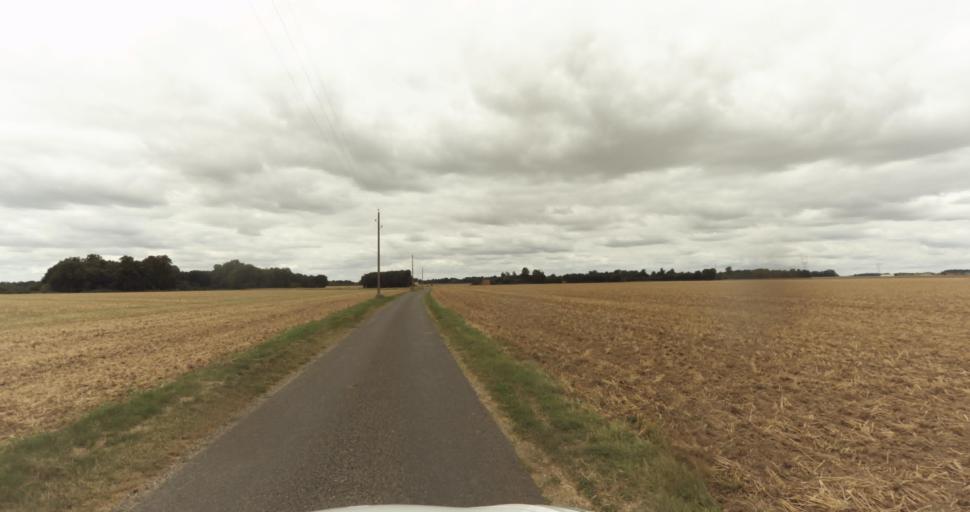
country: FR
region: Haute-Normandie
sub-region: Departement de l'Eure
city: Marcilly-sur-Eure
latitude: 48.8478
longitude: 1.2679
